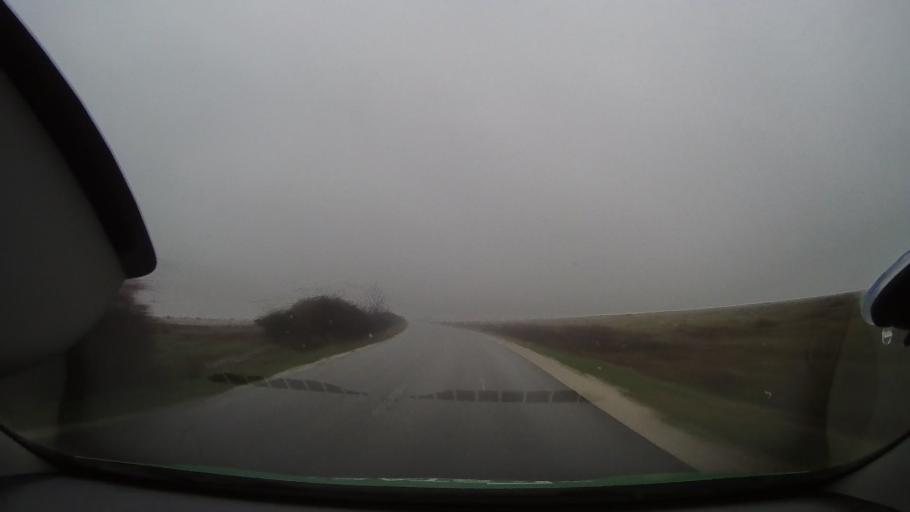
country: RO
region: Arad
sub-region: Comuna Craiova
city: Craiova
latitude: 46.6109
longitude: 21.9566
